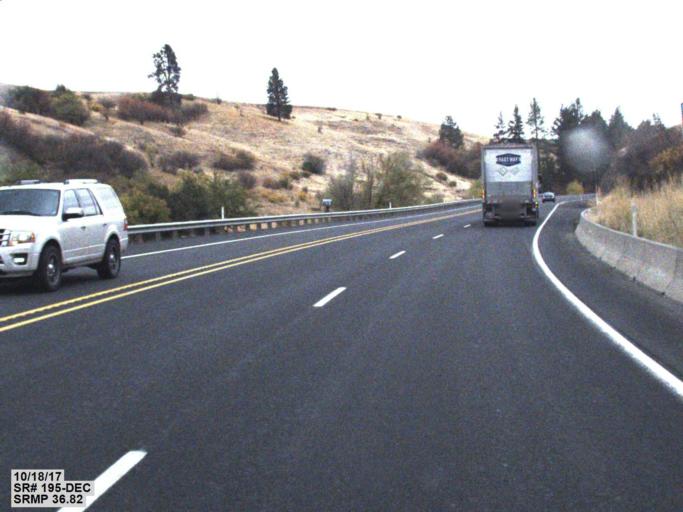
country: US
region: Washington
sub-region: Whitman County
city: Colfax
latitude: 46.8703
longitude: -117.3549
